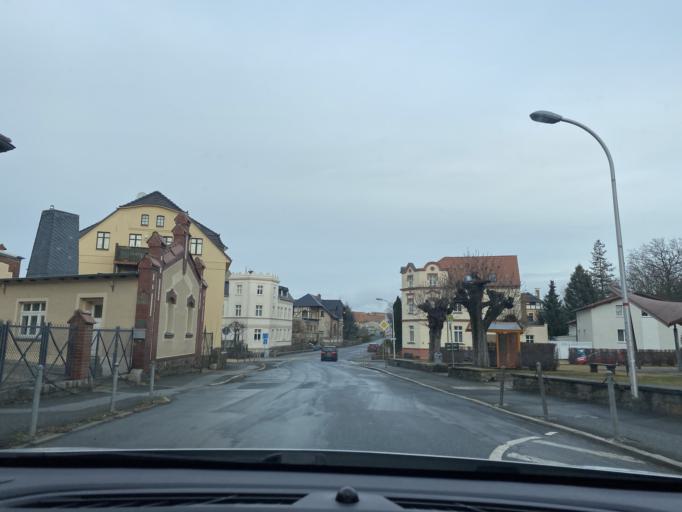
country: DE
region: Saxony
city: Reichenbach
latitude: 51.1388
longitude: 14.7994
